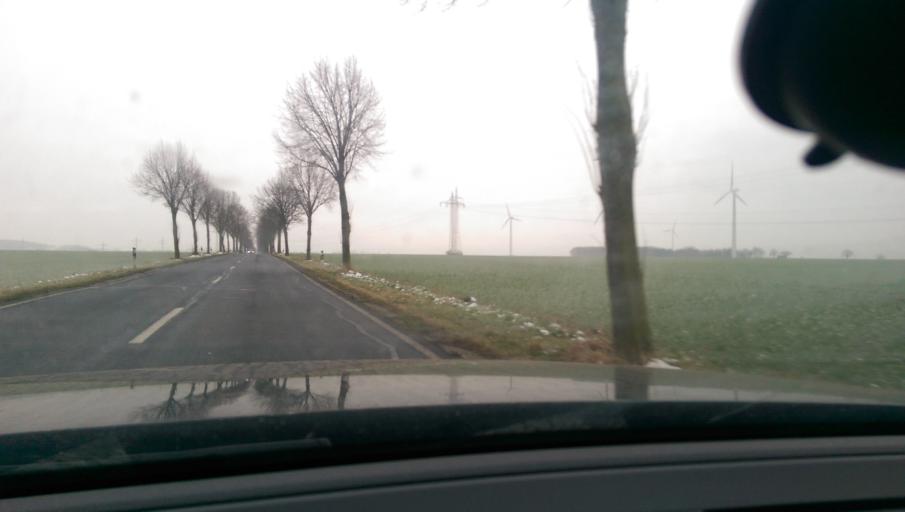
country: DE
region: Lower Saxony
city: Gross Munzel
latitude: 52.3856
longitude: 9.5122
